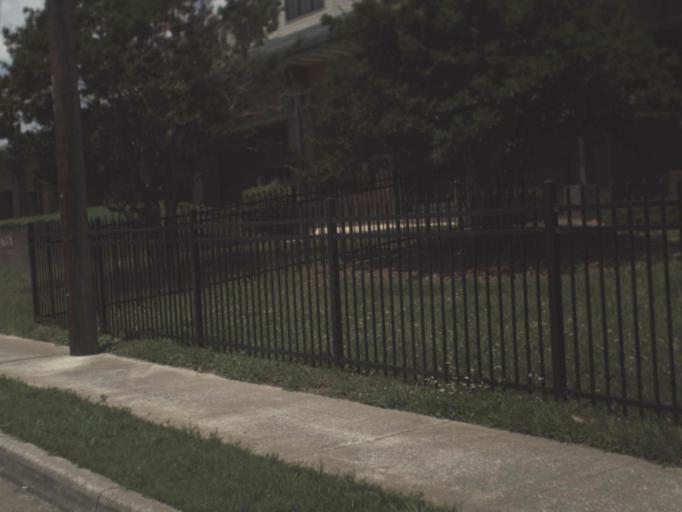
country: US
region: Florida
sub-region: Duval County
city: Jacksonville
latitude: 30.3872
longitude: -81.6858
